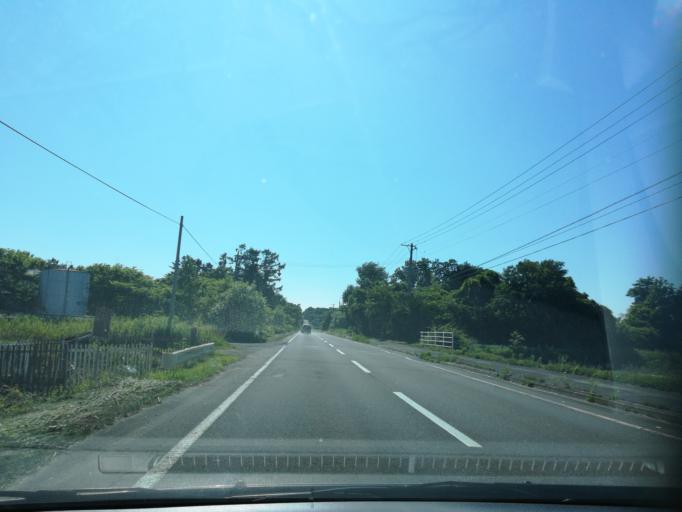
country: JP
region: Hokkaido
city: Chitose
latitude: 42.9149
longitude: 141.8907
